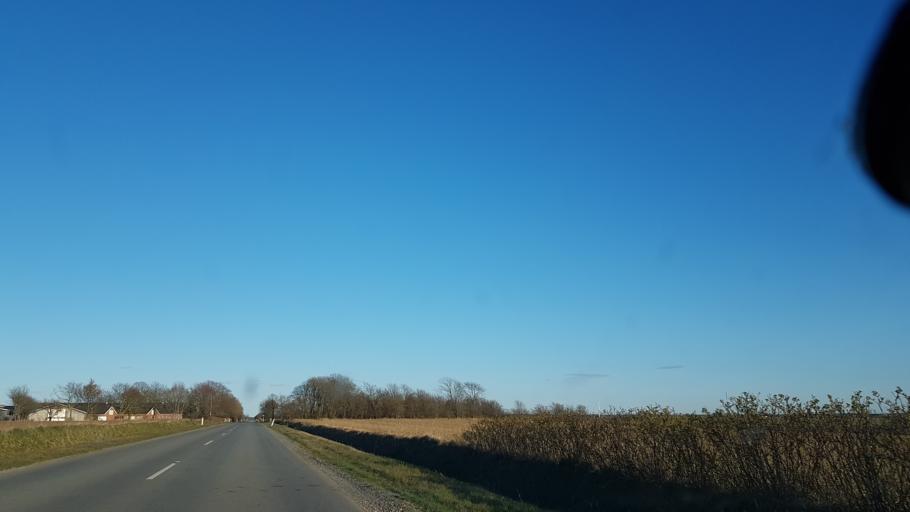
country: DK
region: South Denmark
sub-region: Esbjerg Kommune
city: Bramming
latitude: 55.4229
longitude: 8.6628
